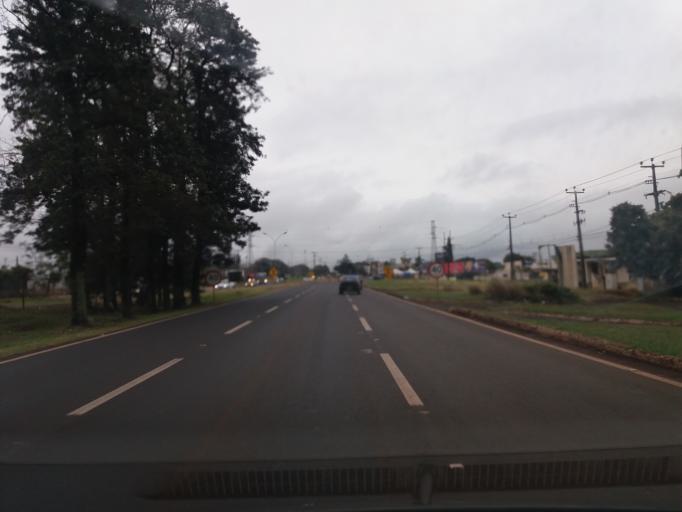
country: BR
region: Parana
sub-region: Maringa
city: Maringa
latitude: -23.4532
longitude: -51.9877
